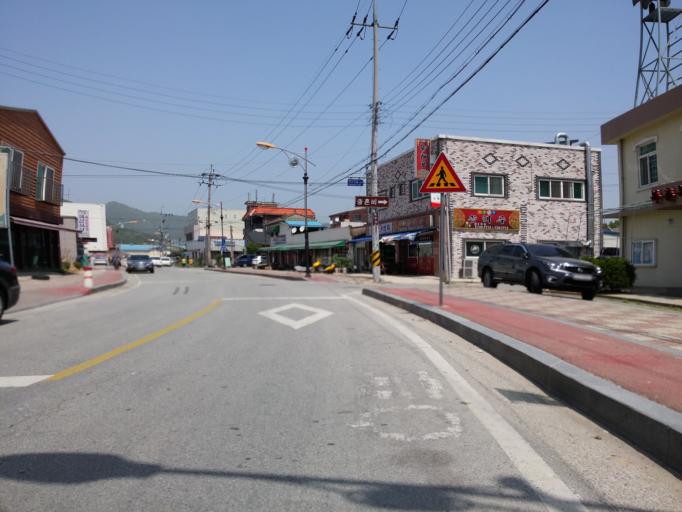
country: KR
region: Chungcheongnam-do
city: Nonsan
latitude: 36.2154
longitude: 127.2176
